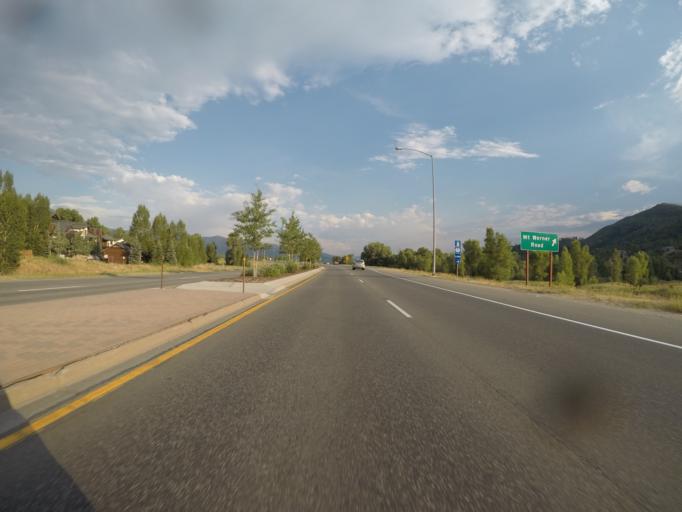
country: US
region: Colorado
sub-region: Routt County
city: Steamboat Springs
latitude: 40.4636
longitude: -106.8256
